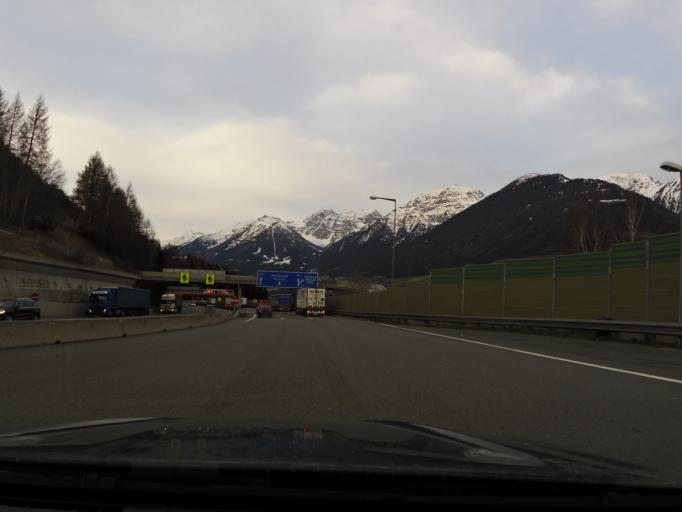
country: AT
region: Tyrol
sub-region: Politischer Bezirk Innsbruck Land
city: Schoenberg im Stubaital
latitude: 47.1847
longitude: 11.4030
